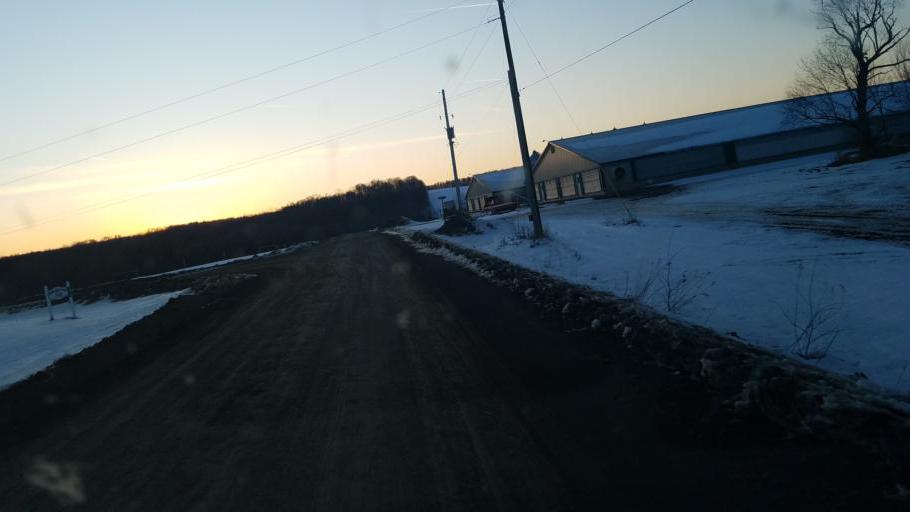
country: US
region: New York
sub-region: Allegany County
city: Andover
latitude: 42.0070
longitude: -77.7186
